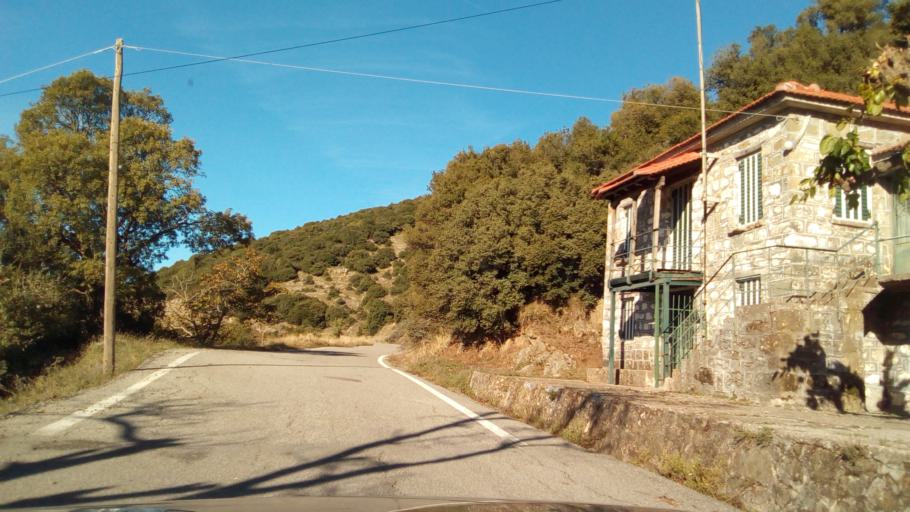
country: GR
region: West Greece
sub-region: Nomos Aitolias kai Akarnanias
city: Nafpaktos
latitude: 38.5020
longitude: 21.8430
